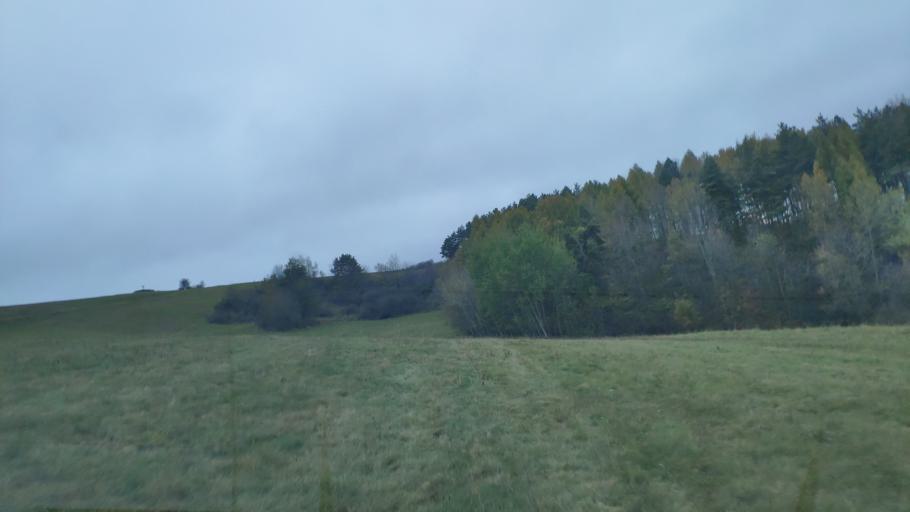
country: SK
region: Presovsky
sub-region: Okres Presov
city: Presov
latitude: 48.9325
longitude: 21.0938
